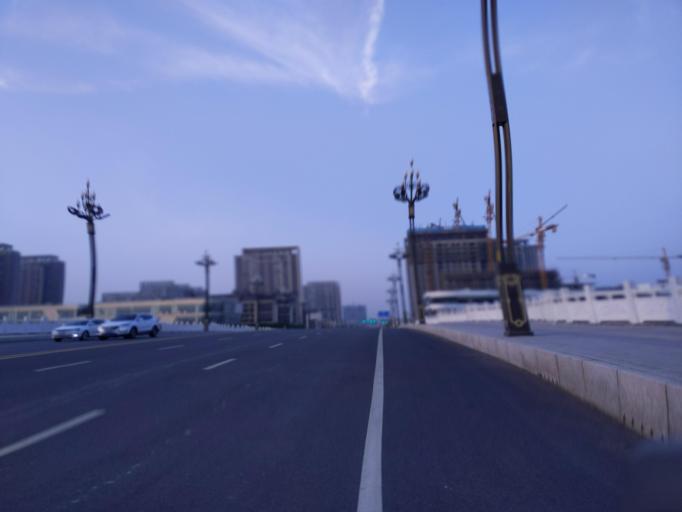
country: CN
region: Henan Sheng
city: Puyang
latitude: 35.8022
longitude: 115.0112
